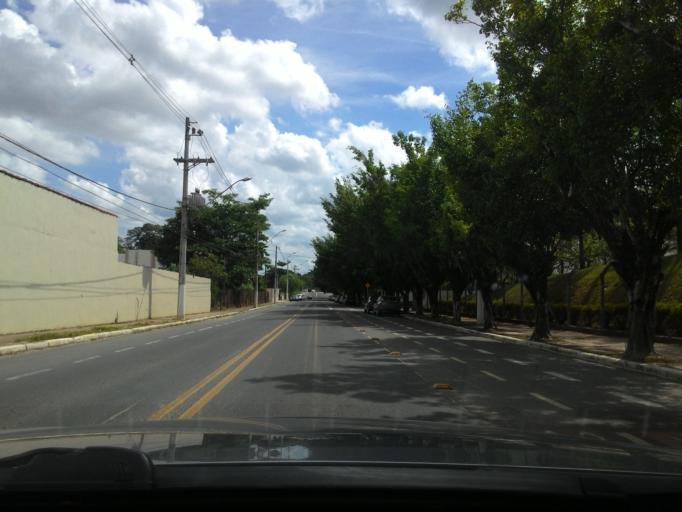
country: BR
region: Sao Paulo
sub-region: Registro
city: Registro
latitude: -24.5034
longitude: -47.8564
